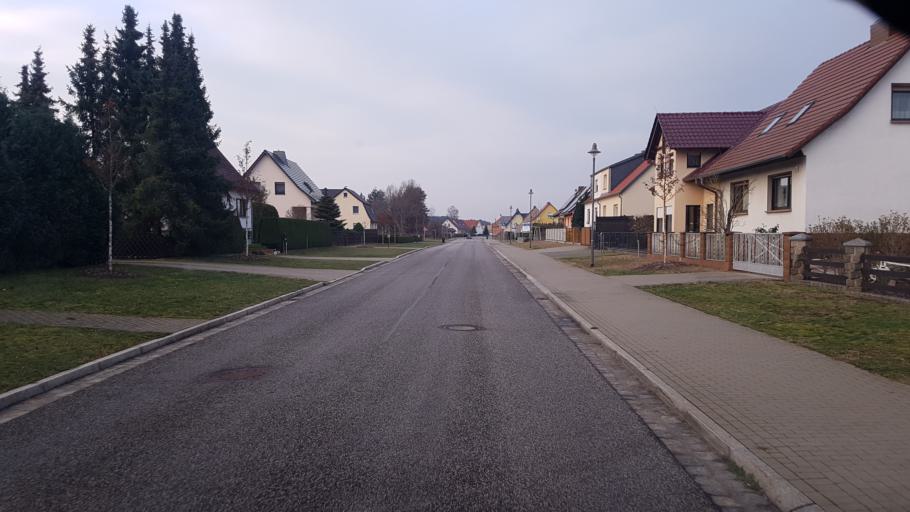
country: DE
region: Brandenburg
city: Ziltendorf
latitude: 52.2014
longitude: 14.6313
